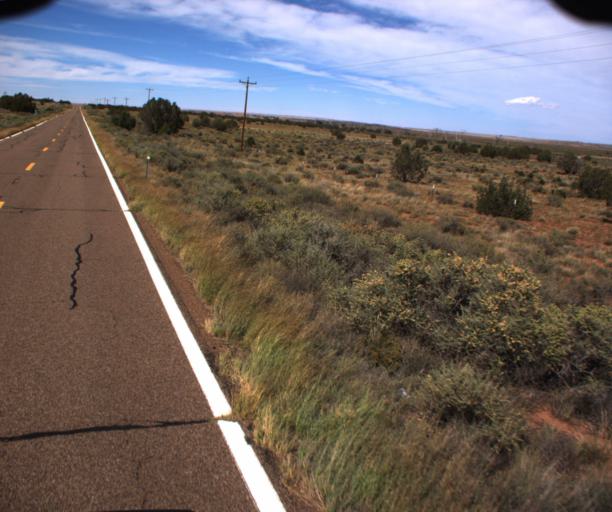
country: US
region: Arizona
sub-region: Apache County
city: Saint Johns
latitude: 34.6070
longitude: -109.6558
